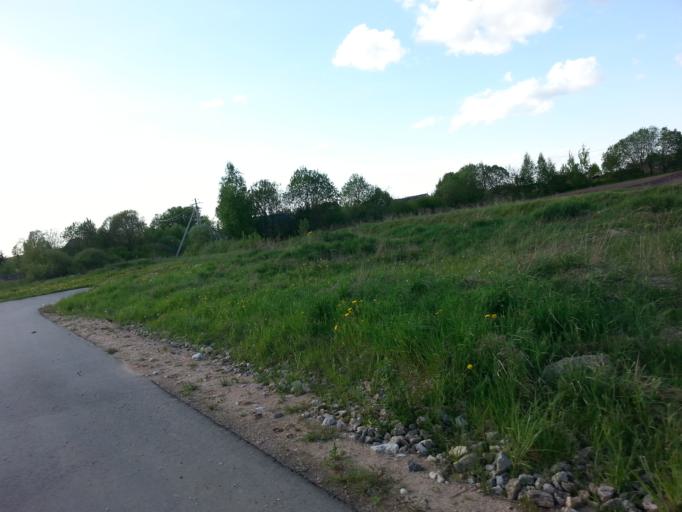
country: BY
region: Minsk
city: Narach
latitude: 54.9406
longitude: 26.6959
